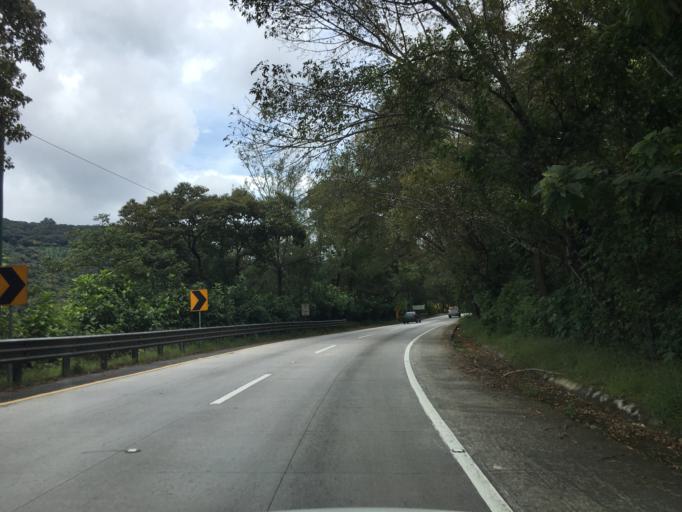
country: GT
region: Sacatepequez
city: Santa Lucia Milpas Altas
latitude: 14.5635
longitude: -90.7000
